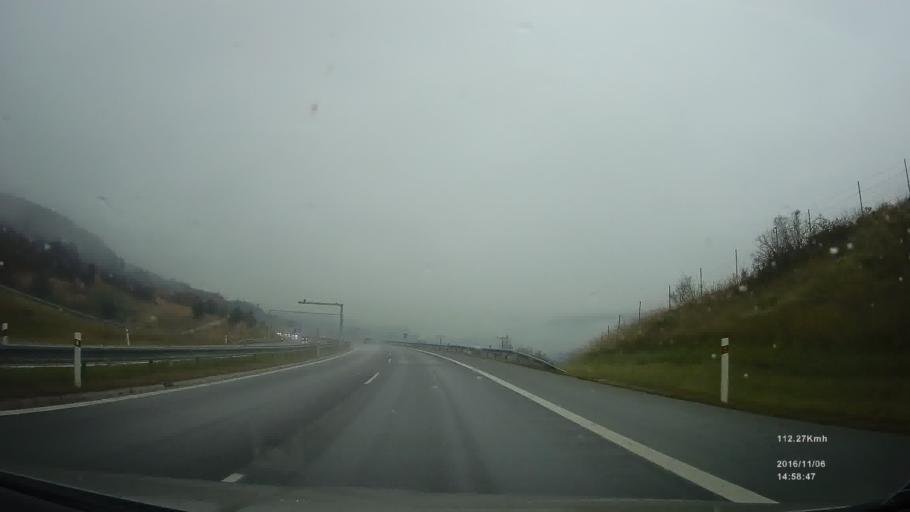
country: SK
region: Kosicky
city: Krompachy
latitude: 49.0150
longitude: 20.9559
